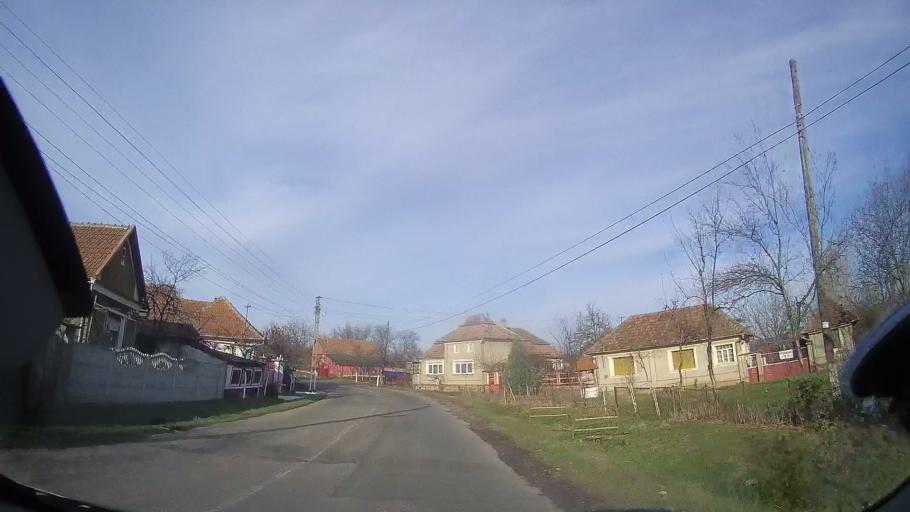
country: RO
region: Bihor
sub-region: Comuna Spinus
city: Spinus
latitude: 47.1770
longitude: 22.2183
